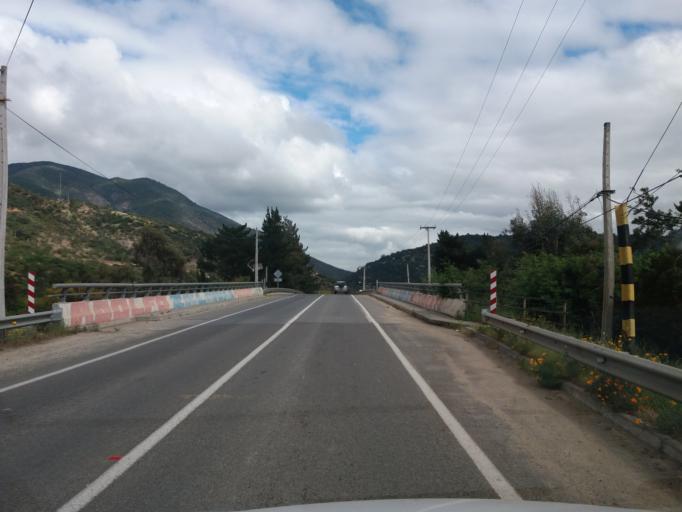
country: CL
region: Valparaiso
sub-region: Provincia de Marga Marga
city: Limache
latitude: -33.0532
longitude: -71.0945
